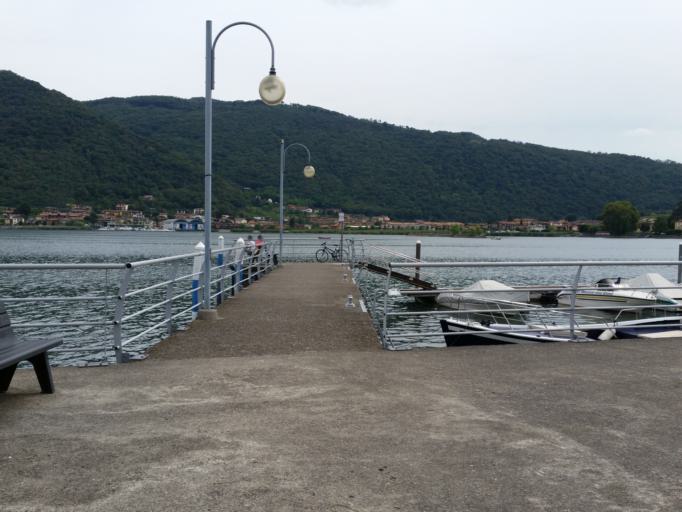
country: IT
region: Lombardy
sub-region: Provincia di Bergamo
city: Sarnico
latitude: 45.6669
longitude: 9.9640
